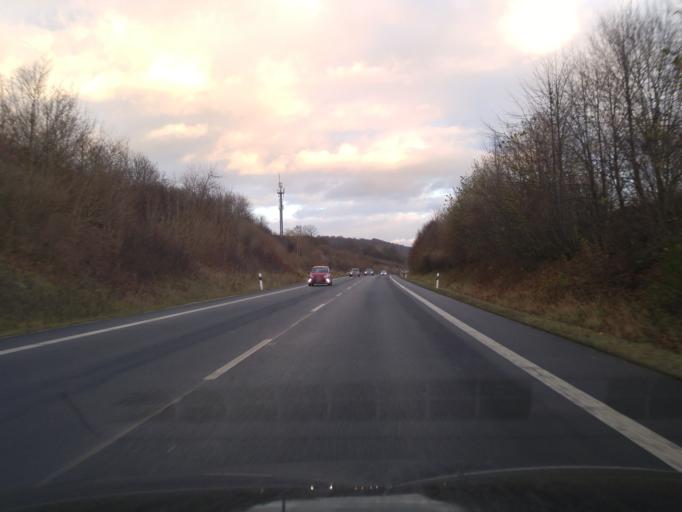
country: DE
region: Lower Saxony
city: Scheden
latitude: 51.3953
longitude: 9.7716
